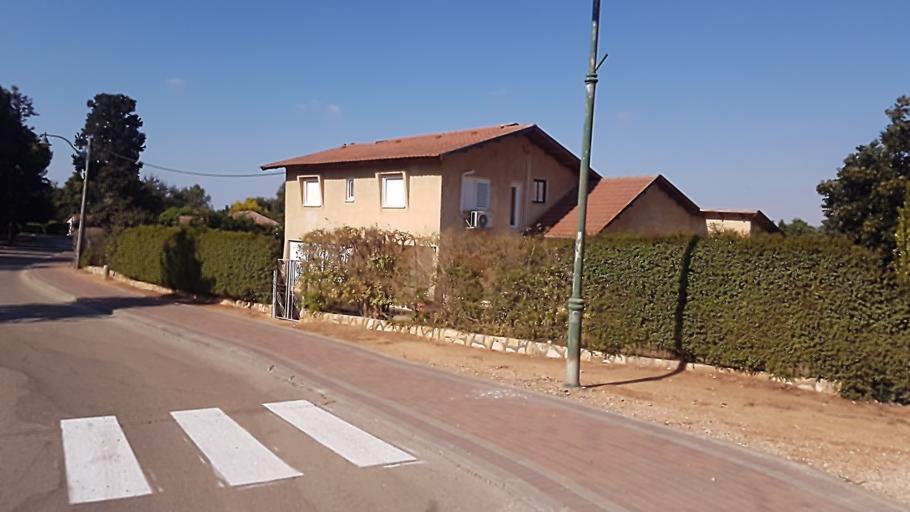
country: IL
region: Central District
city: Kfar Saba
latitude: 32.2100
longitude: 34.9017
